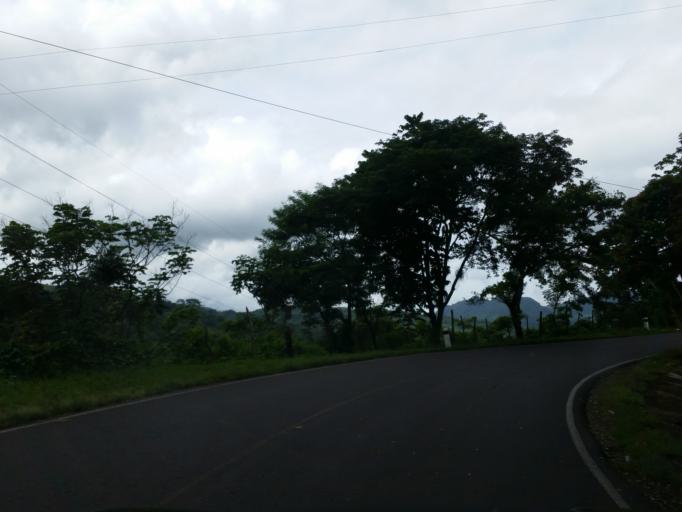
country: NI
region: Matagalpa
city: San Ramon
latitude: 13.0058
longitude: -85.8004
